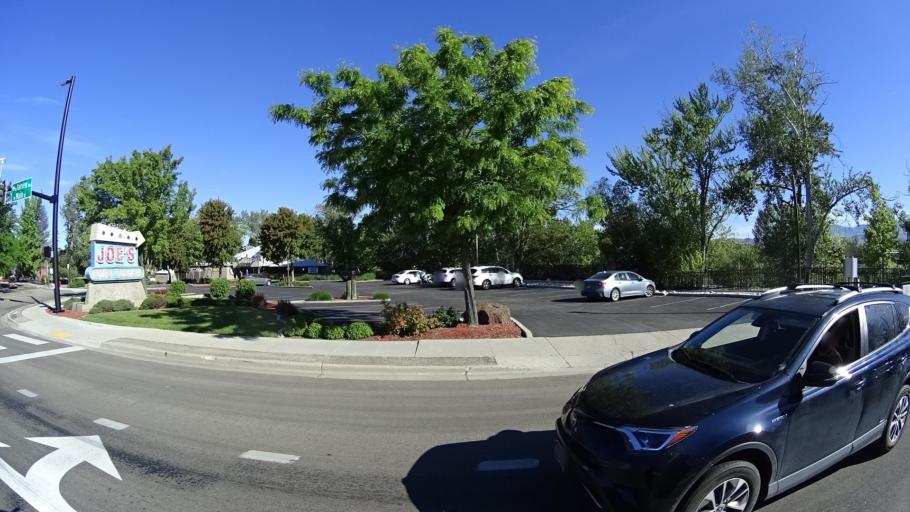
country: US
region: Idaho
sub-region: Ada County
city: Garden City
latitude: 43.6202
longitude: -116.2316
